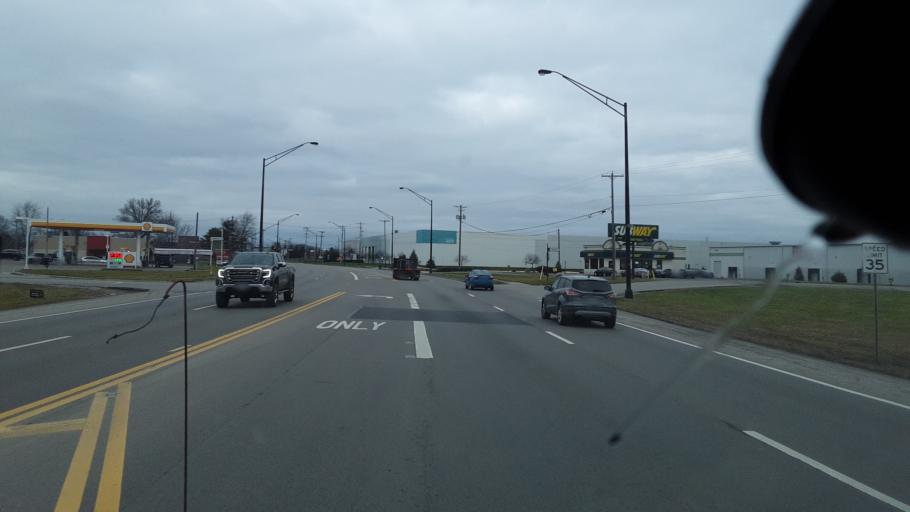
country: US
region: Ohio
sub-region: Franklin County
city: Obetz
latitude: 39.8762
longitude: -82.9315
